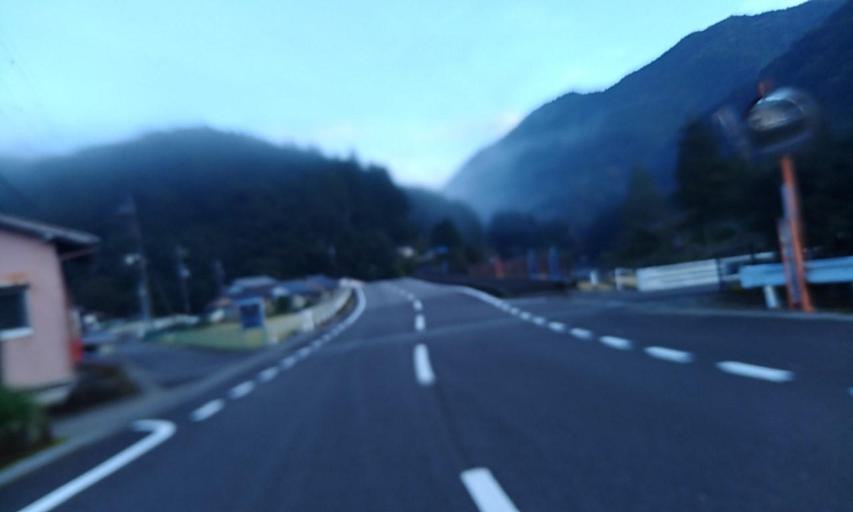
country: JP
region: Wakayama
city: Shingu
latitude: 33.7286
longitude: 135.9100
